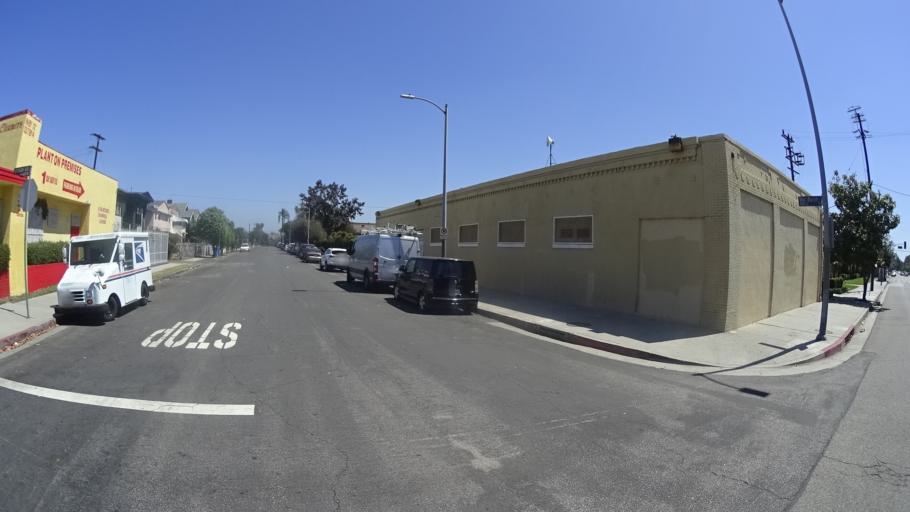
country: US
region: California
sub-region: Los Angeles County
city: View Park-Windsor Hills
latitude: 34.0256
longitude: -118.2971
